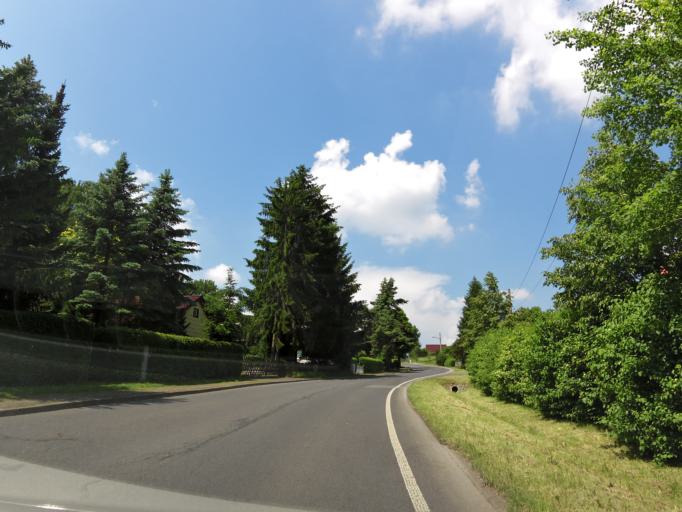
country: DE
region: Thuringia
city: Waltershausen
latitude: 50.8958
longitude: 10.5455
